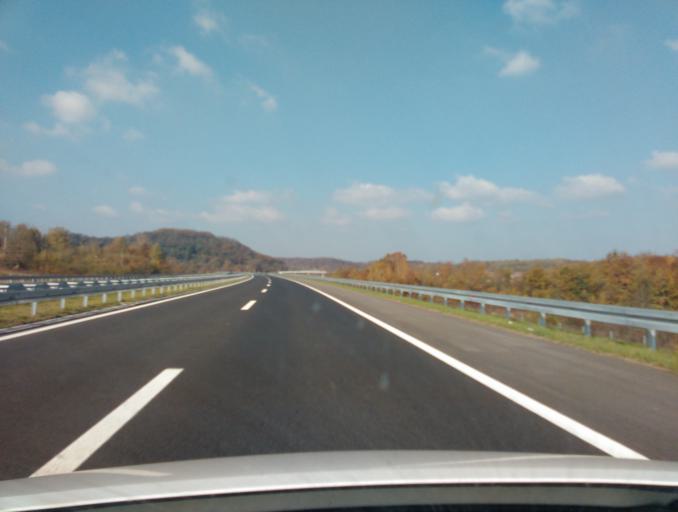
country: BA
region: Republika Srpska
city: Prnjavor
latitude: 44.8849
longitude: 17.6166
